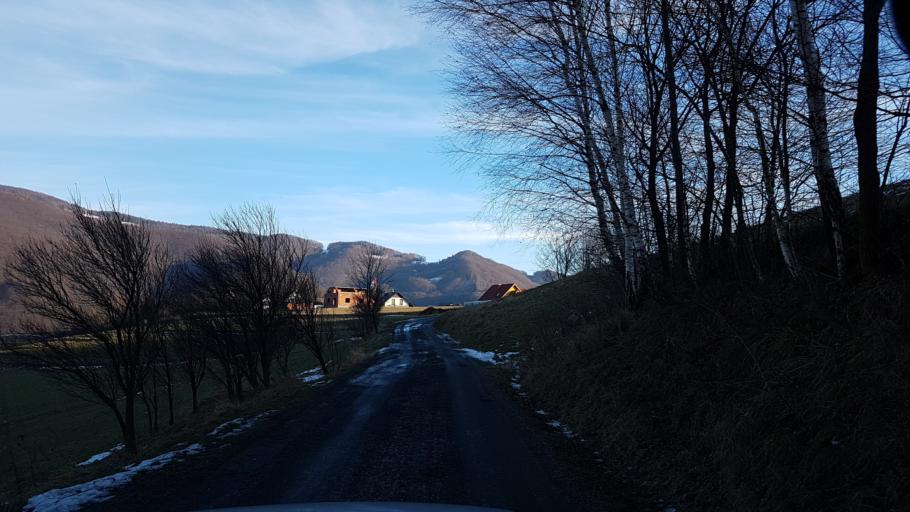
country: PL
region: Lesser Poland Voivodeship
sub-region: Powiat nowosadecki
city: Rytro
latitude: 49.4950
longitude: 20.6702
